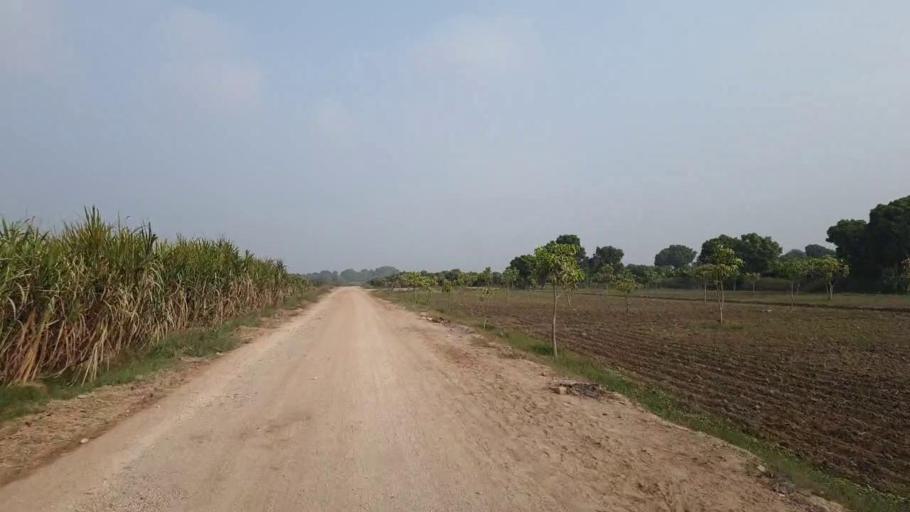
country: PK
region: Sindh
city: Tando Muhammad Khan
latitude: 25.1640
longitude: 68.5934
